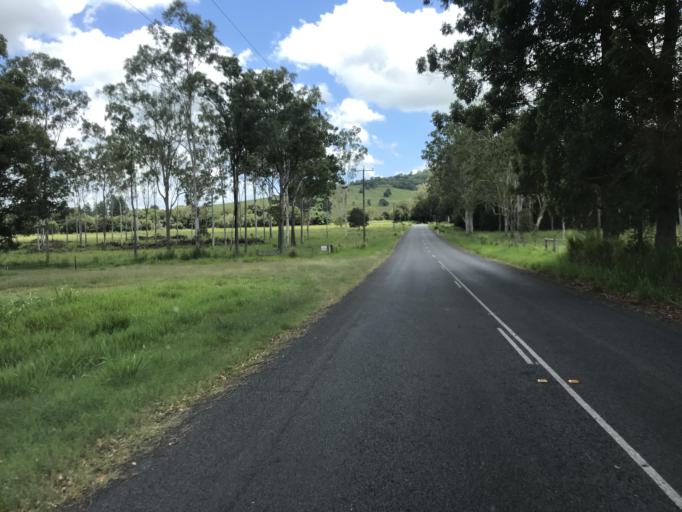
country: AU
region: Queensland
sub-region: Tablelands
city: Atherton
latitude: -17.3010
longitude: 145.5591
